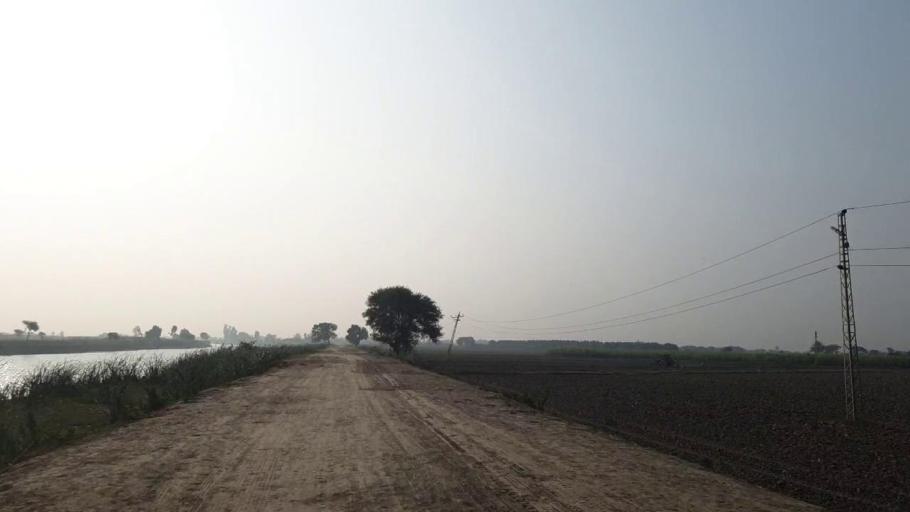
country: PK
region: Sindh
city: Tando Muhammad Khan
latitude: 25.0973
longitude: 68.5763
